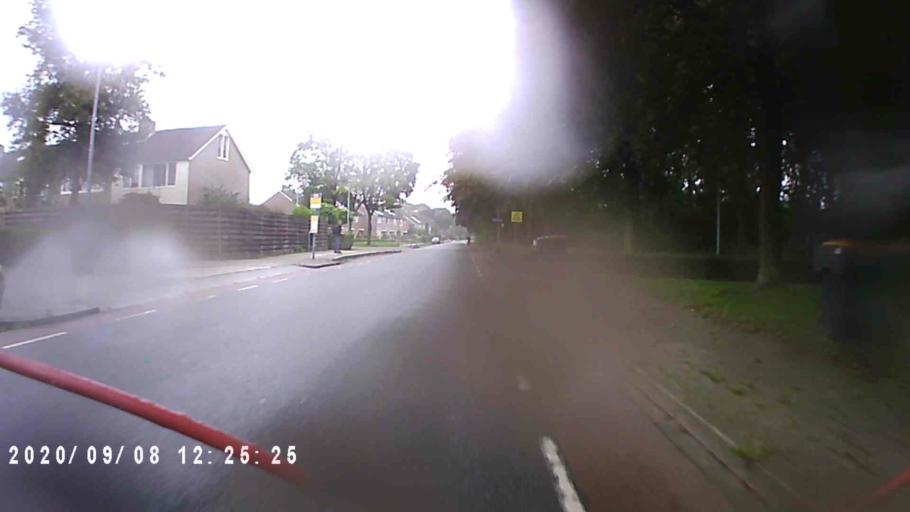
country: NL
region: Groningen
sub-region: Gemeente Veendam
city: Veendam
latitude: 53.0966
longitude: 6.8669
